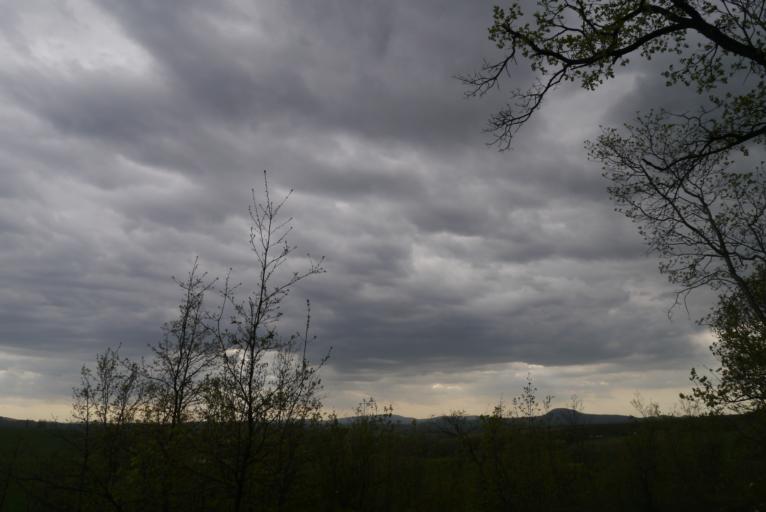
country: HU
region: Komarom-Esztergom
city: Piliscsev
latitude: 47.6824
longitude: 18.8391
